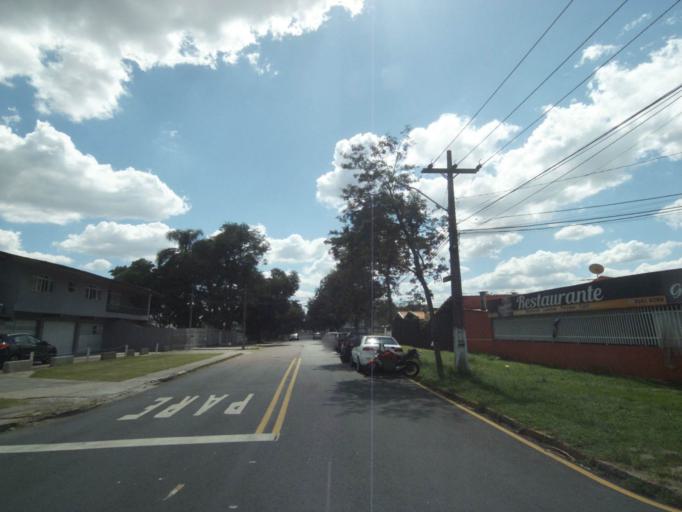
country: BR
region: Parana
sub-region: Pinhais
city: Pinhais
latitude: -25.4339
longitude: -49.2134
